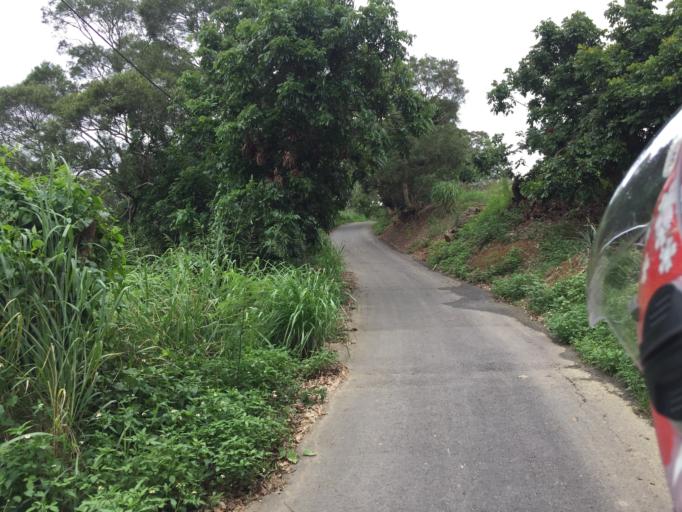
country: TW
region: Taiwan
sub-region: Taichung City
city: Taichung
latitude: 24.0660
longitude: 120.7136
